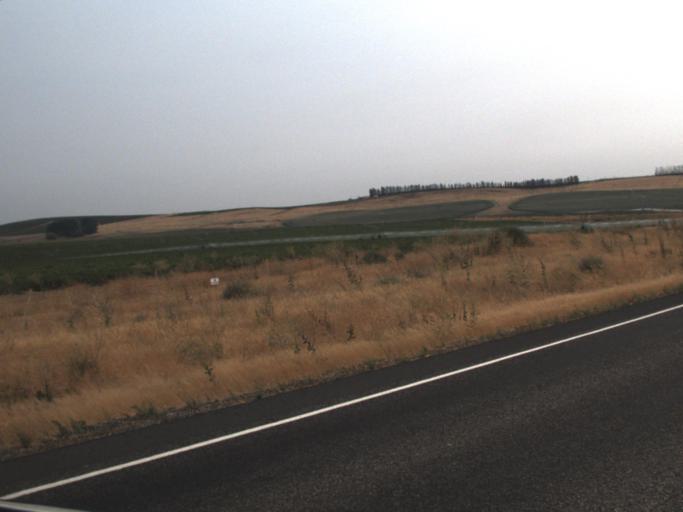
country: US
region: Oregon
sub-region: Morrow County
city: Irrigon
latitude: 45.9819
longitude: -119.6030
